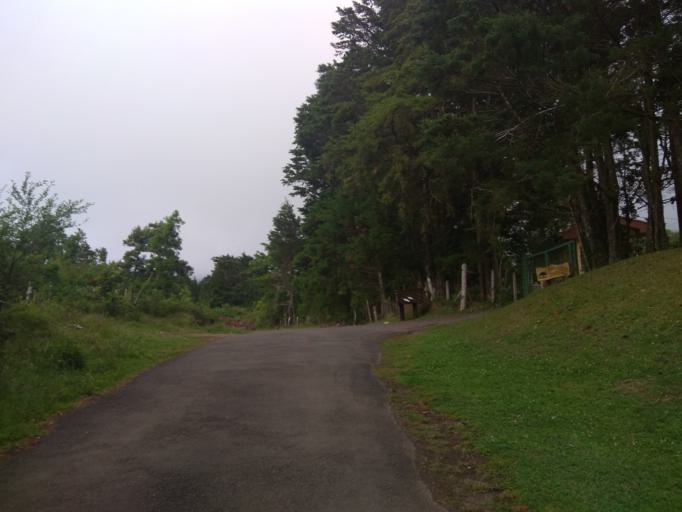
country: CR
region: Heredia
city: San Josecito
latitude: 10.0712
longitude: -84.0831
